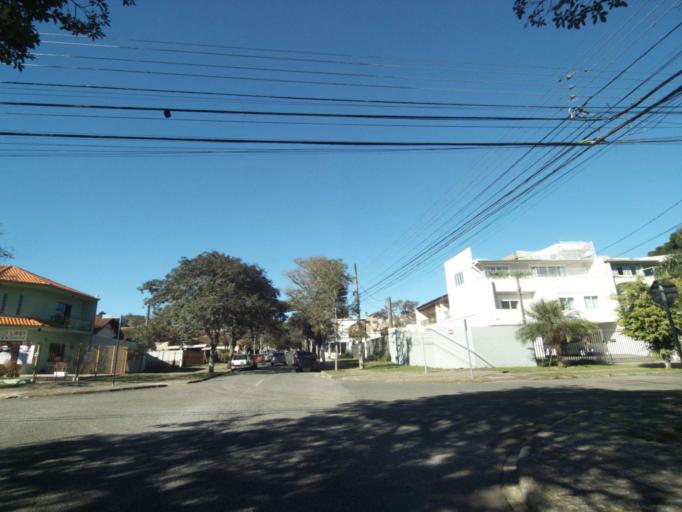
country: BR
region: Parana
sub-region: Curitiba
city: Curitiba
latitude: -25.4188
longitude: -49.2469
